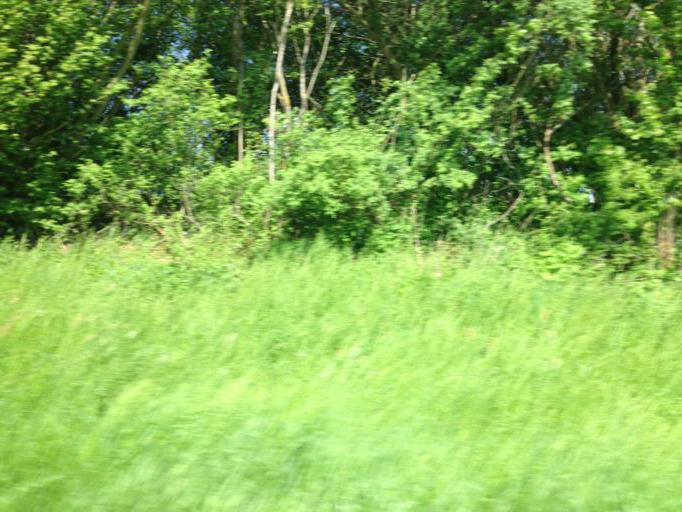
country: DE
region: North Rhine-Westphalia
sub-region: Regierungsbezirk Koln
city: Mechernich
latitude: 50.5670
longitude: 6.7004
